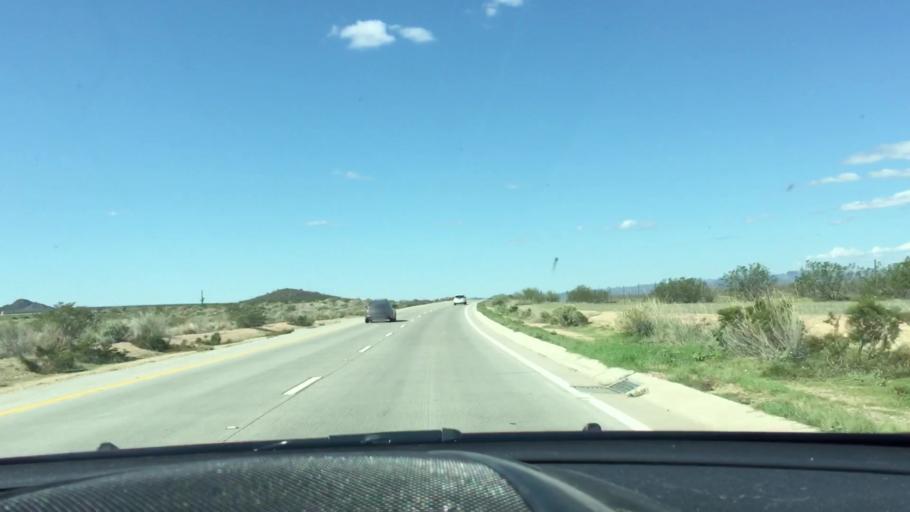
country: US
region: Arizona
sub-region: Maricopa County
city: Anthem
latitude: 33.7707
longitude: -112.1708
